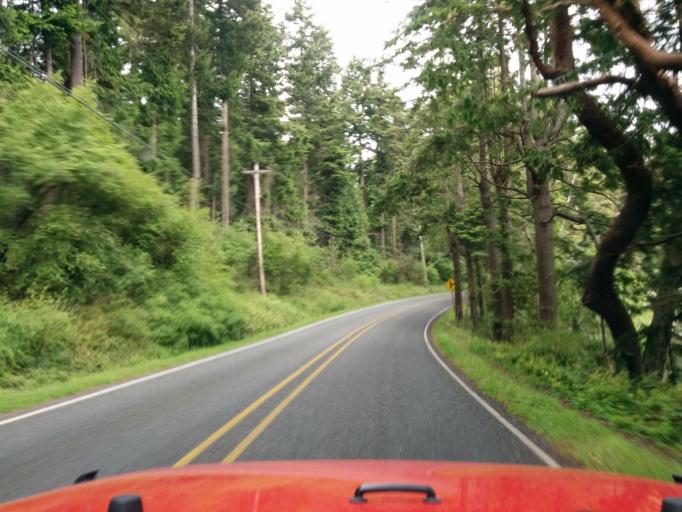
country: US
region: Washington
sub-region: Island County
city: Coupeville
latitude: 48.2204
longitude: -122.7301
